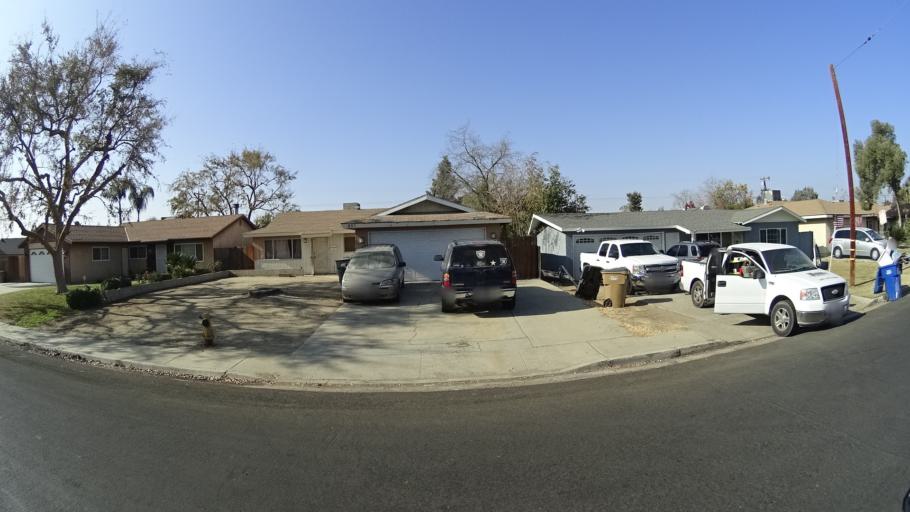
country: US
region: California
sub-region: Kern County
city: Bakersfield
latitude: 35.3484
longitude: -119.0344
